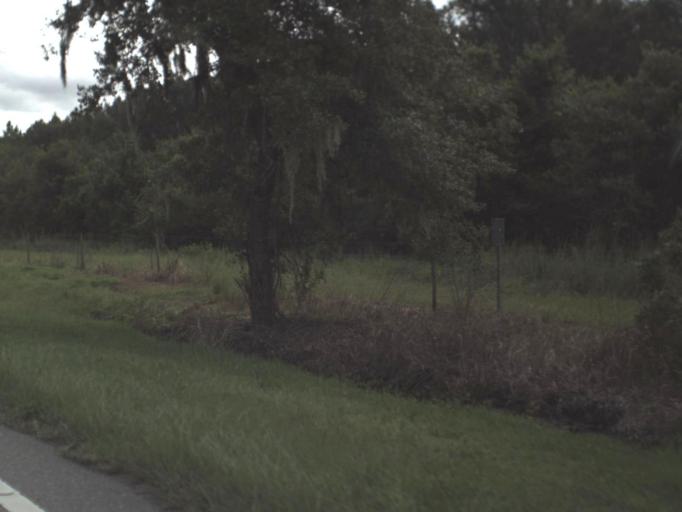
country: US
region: Florida
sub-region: Hillsborough County
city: Wimauma
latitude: 27.5949
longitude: -82.1136
